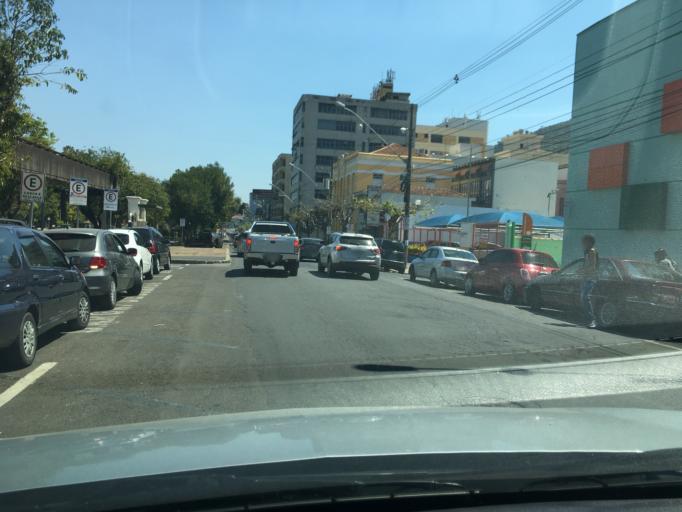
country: BR
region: Minas Gerais
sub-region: Pocos De Caldas
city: Pocos de Caldas
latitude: -21.7854
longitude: -46.5665
